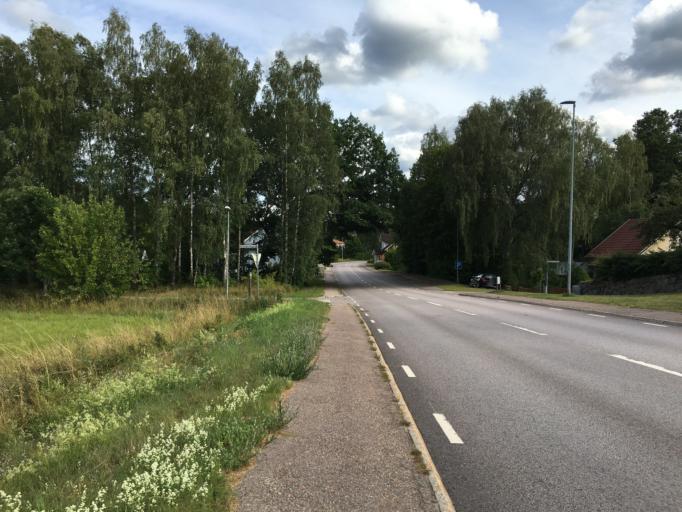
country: SE
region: Kalmar
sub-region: Nybro Kommun
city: Nybro
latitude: 56.9453
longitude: 15.9121
